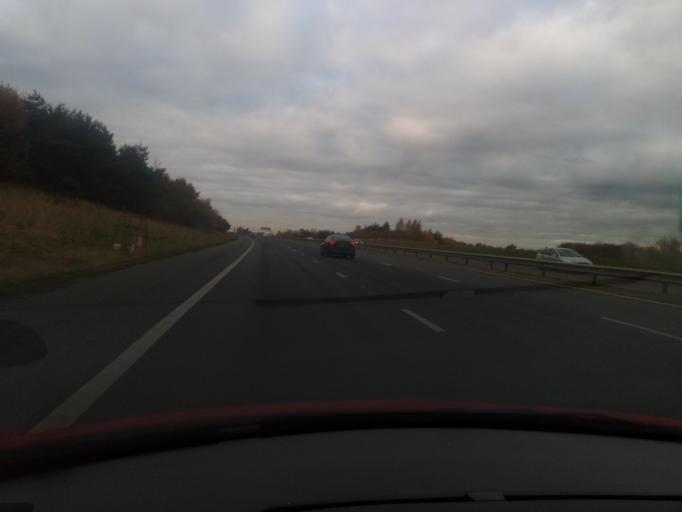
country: GB
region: England
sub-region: North Yorkshire
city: Boroughbridge
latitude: 54.1475
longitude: -1.4339
